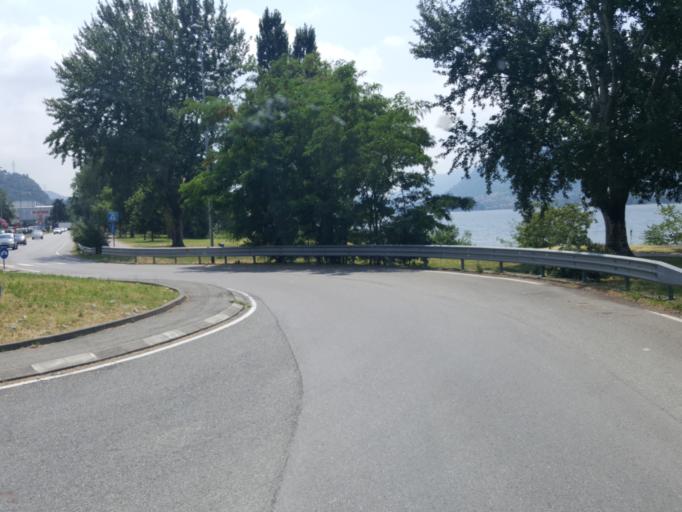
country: IT
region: Lombardy
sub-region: Provincia di Lecco
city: Pescate
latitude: 45.8299
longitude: 9.4090
